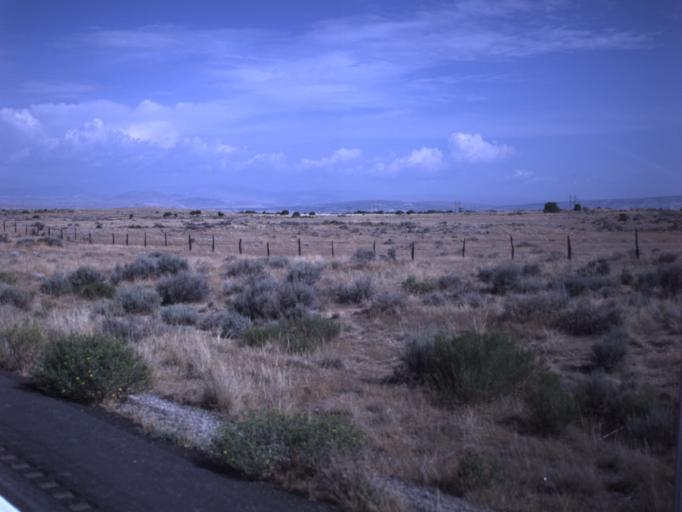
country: US
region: Utah
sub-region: Uintah County
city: Naples
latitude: 40.3280
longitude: -109.2734
